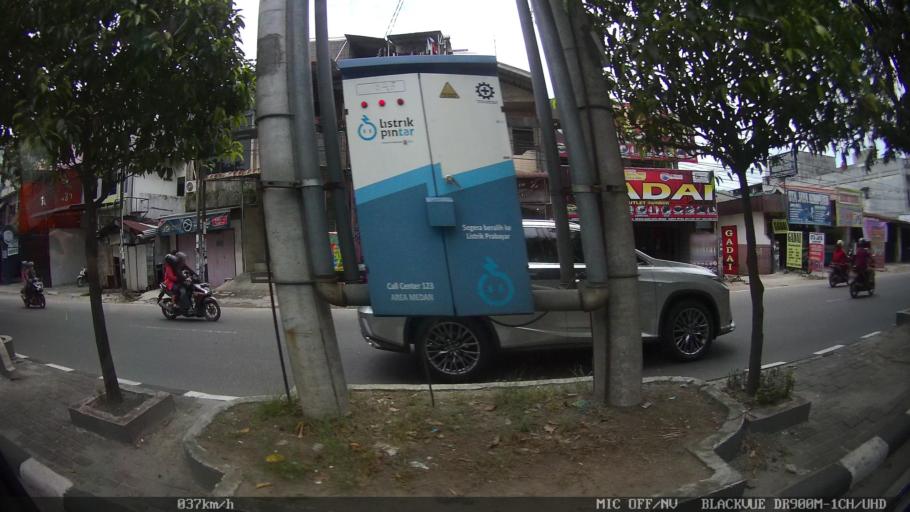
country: ID
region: North Sumatra
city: Medan
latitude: 3.5568
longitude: 98.6621
